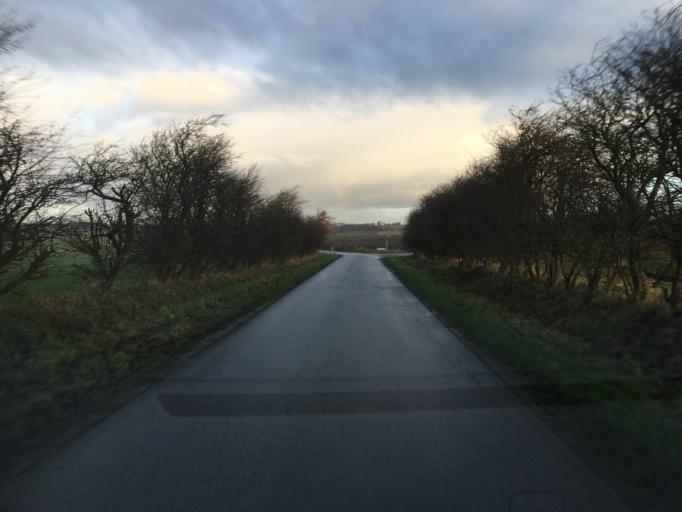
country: DK
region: South Denmark
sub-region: Tonder Kommune
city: Sherrebek
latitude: 55.1347
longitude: 8.8282
